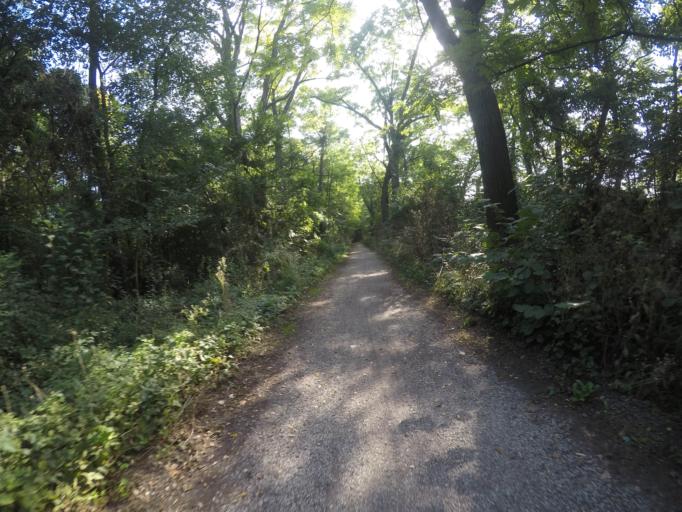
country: SK
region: Trnavsky
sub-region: Okres Dunajska Streda
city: Velky Meder
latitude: 47.8448
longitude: 17.7530
